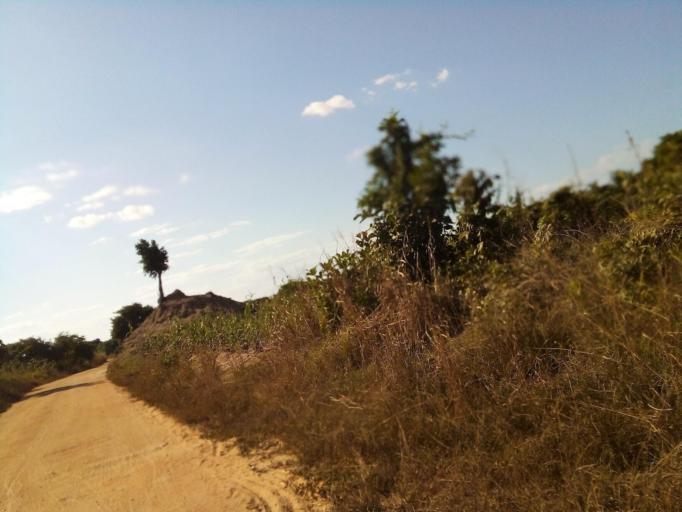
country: MZ
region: Zambezia
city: Quelimane
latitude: -17.5590
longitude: 36.6357
